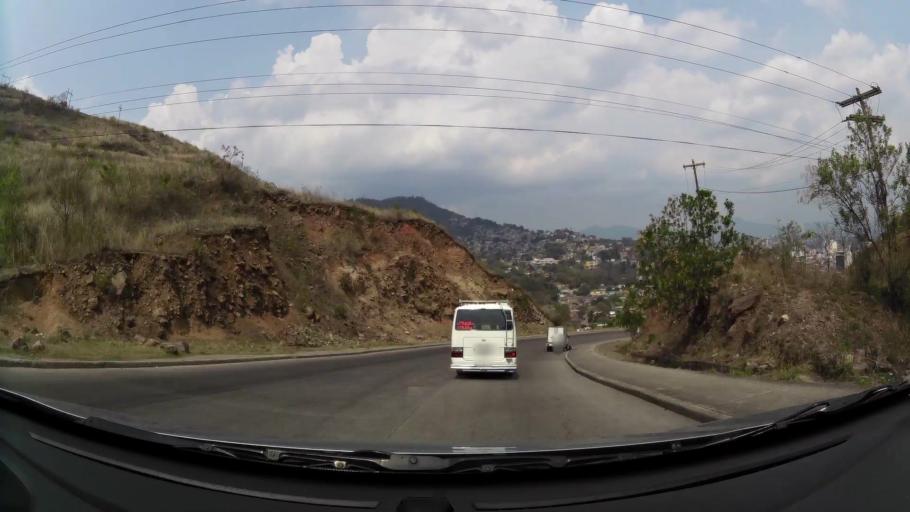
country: HN
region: Francisco Morazan
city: Tegucigalpa
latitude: 14.1138
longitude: -87.2143
